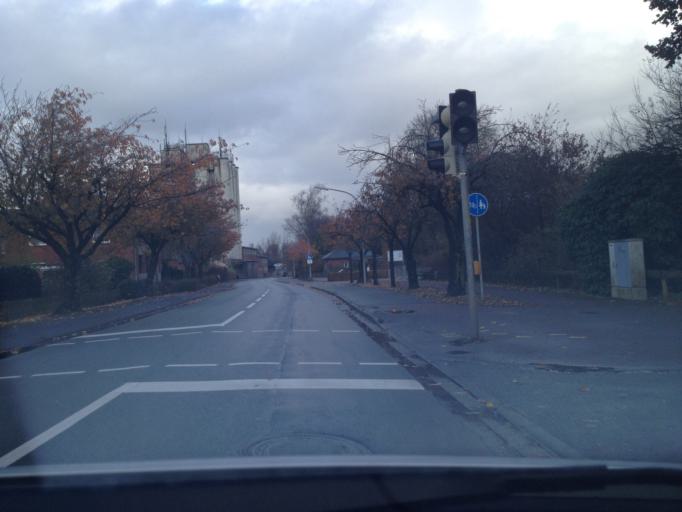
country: DE
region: Schleswig-Holstein
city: Leck
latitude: 54.7743
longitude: 8.9764
